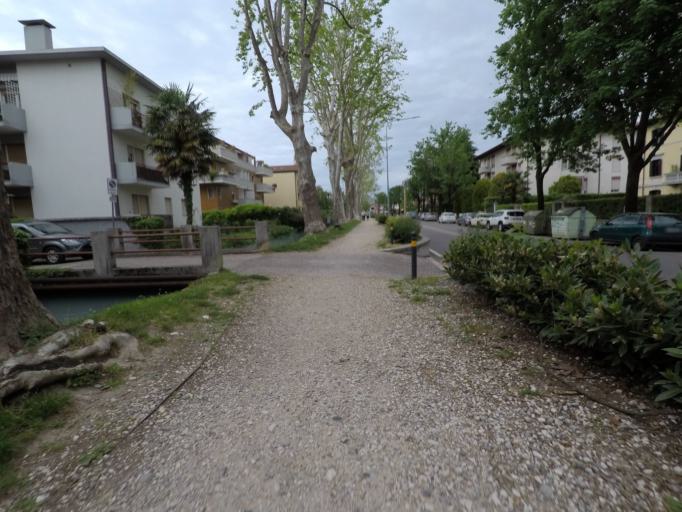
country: IT
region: Friuli Venezia Giulia
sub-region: Provincia di Udine
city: Udine
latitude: 46.0793
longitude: 13.2360
